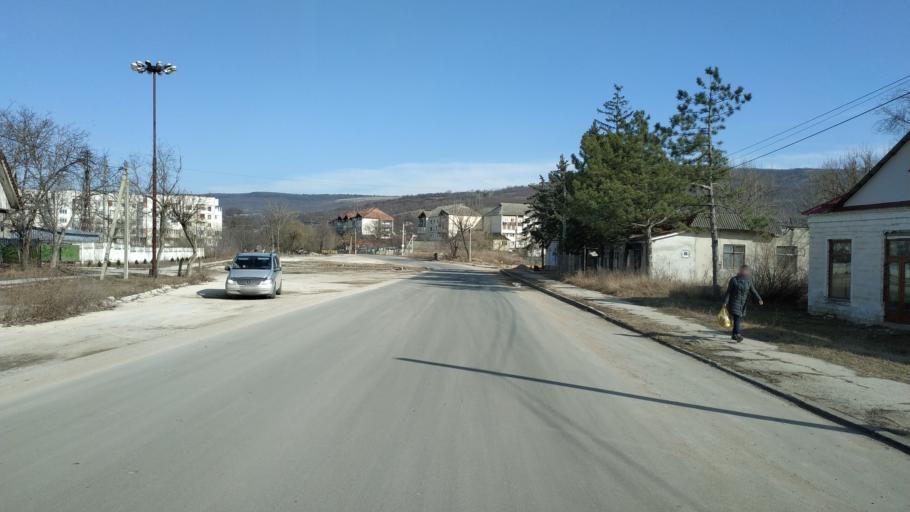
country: MD
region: Nisporeni
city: Nisporeni
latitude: 47.0730
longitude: 28.1774
